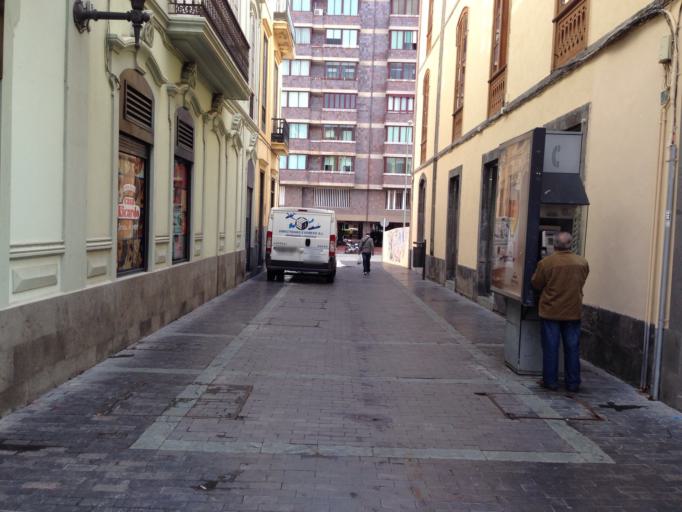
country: ES
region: Canary Islands
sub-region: Provincia de Las Palmas
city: Las Palmas de Gran Canaria
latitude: 28.1067
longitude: -15.4167
